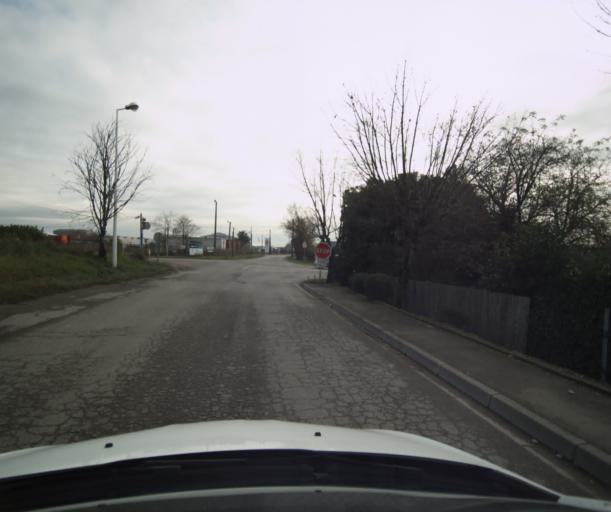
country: FR
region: Midi-Pyrenees
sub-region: Departement de la Haute-Garonne
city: Lespinasse
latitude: 43.7128
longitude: 1.3972
